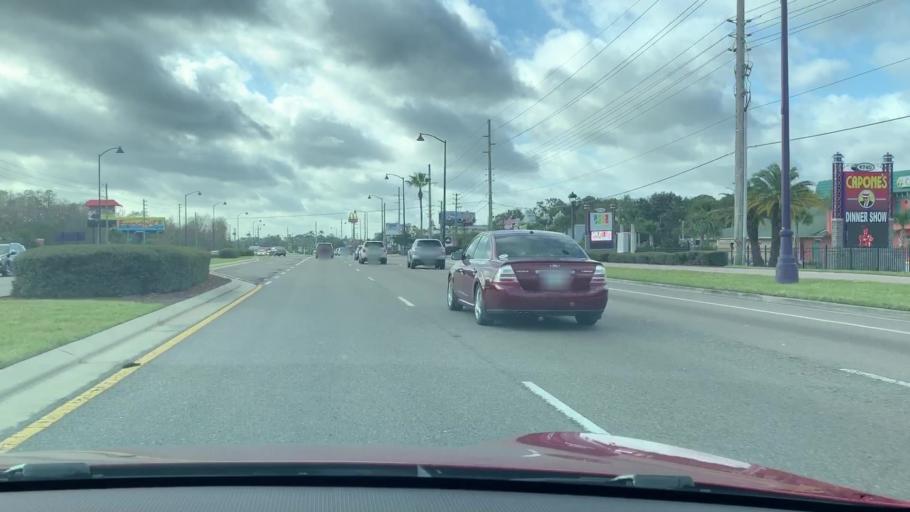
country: US
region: Florida
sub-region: Osceola County
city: Kissimmee
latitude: 28.3248
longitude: -81.4708
